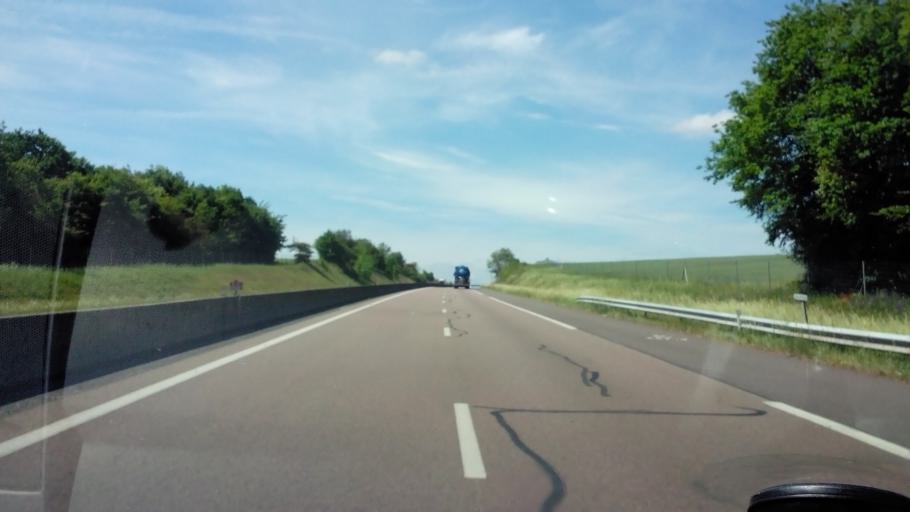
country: FR
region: Lorraine
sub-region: Departement de Meurthe-et-Moselle
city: Colombey-les-Belles
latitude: 48.4797
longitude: 5.8928
